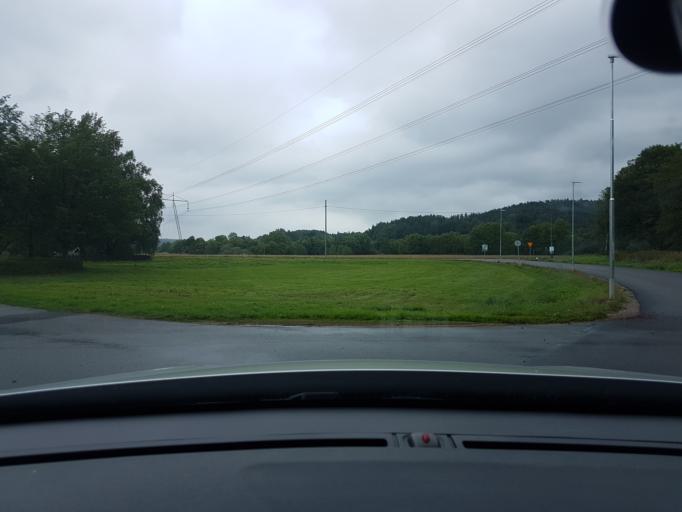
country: SE
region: Vaestra Goetaland
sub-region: Ale Kommun
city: Salanda
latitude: 57.9816
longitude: 12.2229
